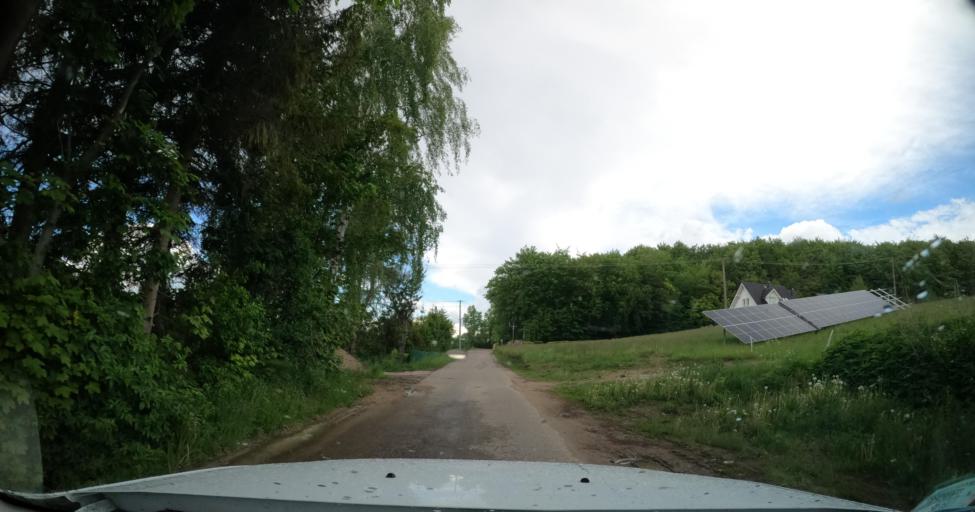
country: PL
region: Pomeranian Voivodeship
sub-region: Powiat kartuski
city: Garcz
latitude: 54.3427
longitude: 18.1456
